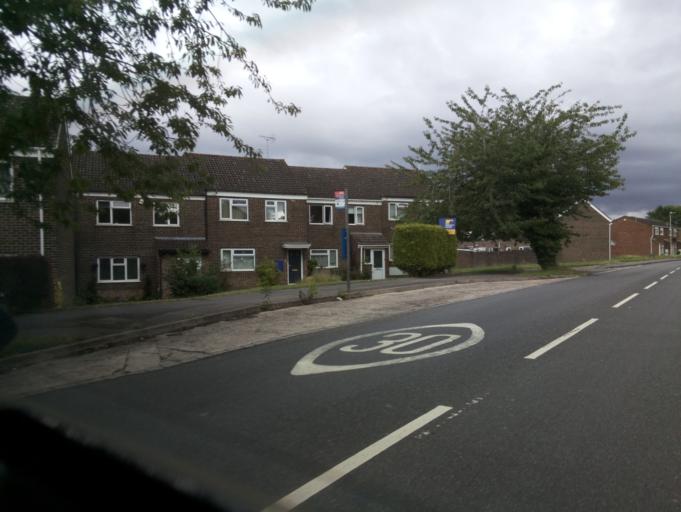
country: GB
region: England
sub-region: Gloucestershire
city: Gloucester
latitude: 51.8435
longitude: -2.2294
